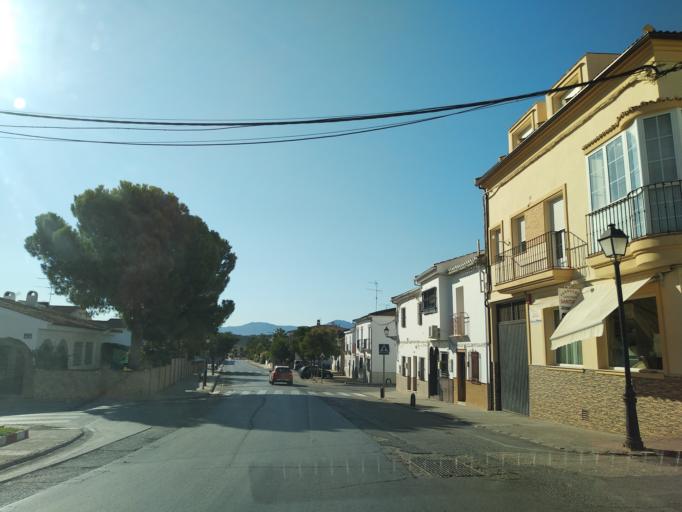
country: ES
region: Andalusia
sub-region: Provincia de Malaga
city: Mollina
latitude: 37.1233
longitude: -4.6611
